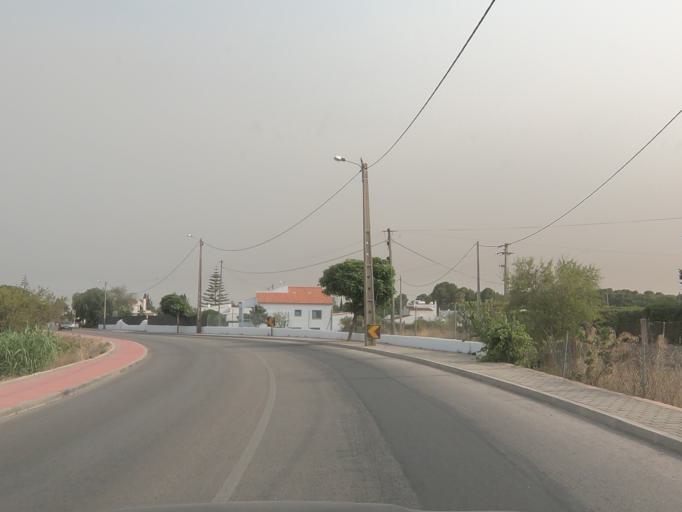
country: PT
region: Faro
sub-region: Silves
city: Armacao de Pera
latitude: 37.1191
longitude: -8.4013
